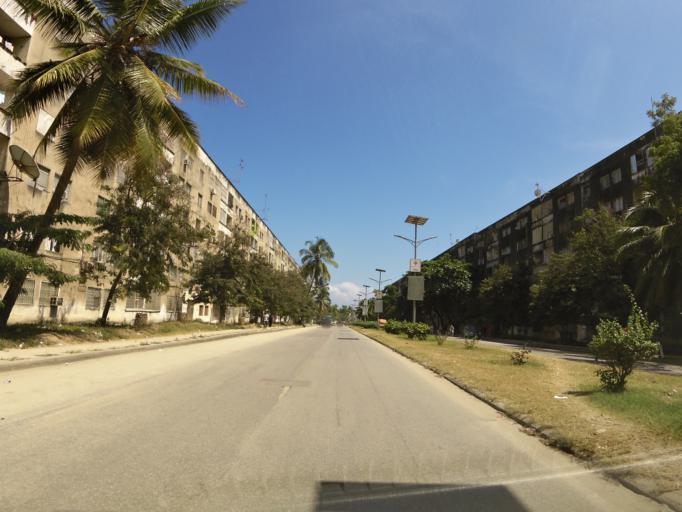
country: TZ
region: Zanzibar Urban/West
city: Zanzibar
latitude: -6.1651
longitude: 39.1981
